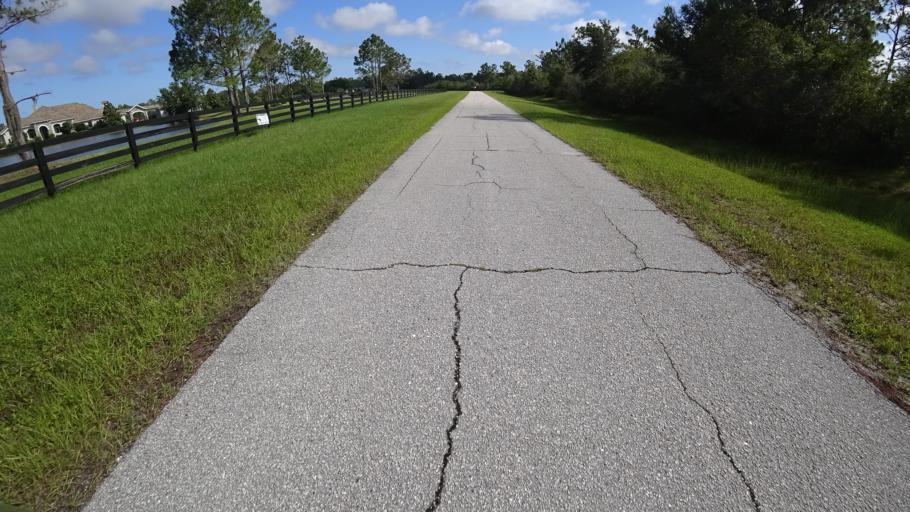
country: US
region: Florida
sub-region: Sarasota County
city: The Meadows
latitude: 27.4024
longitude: -82.3285
